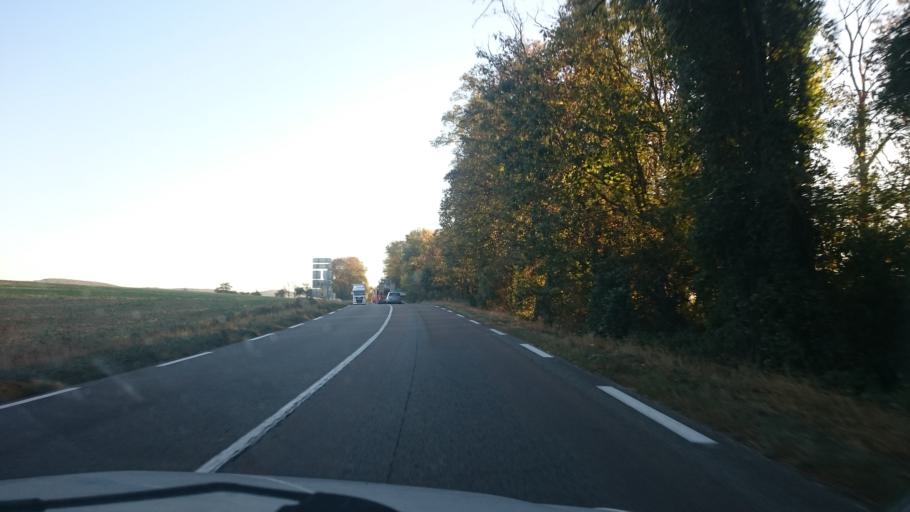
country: FR
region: Franche-Comte
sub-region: Departement du Doubs
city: Quingey
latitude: 47.0763
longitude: 5.8826
